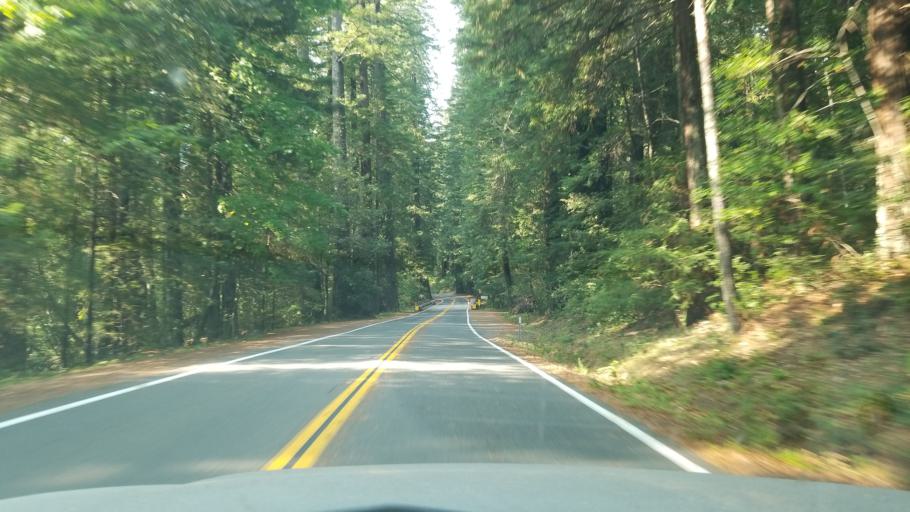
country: US
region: California
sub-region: Humboldt County
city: Redway
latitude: 40.2769
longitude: -123.8526
